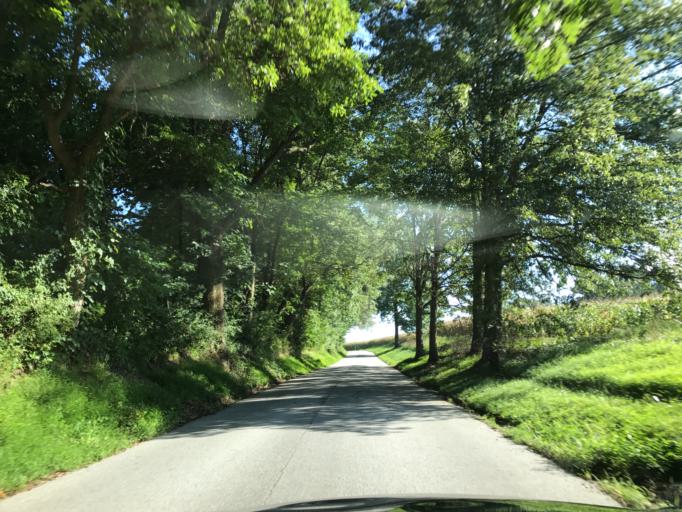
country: US
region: Maryland
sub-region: Harford County
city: Jarrettsville
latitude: 39.6211
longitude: -76.6005
